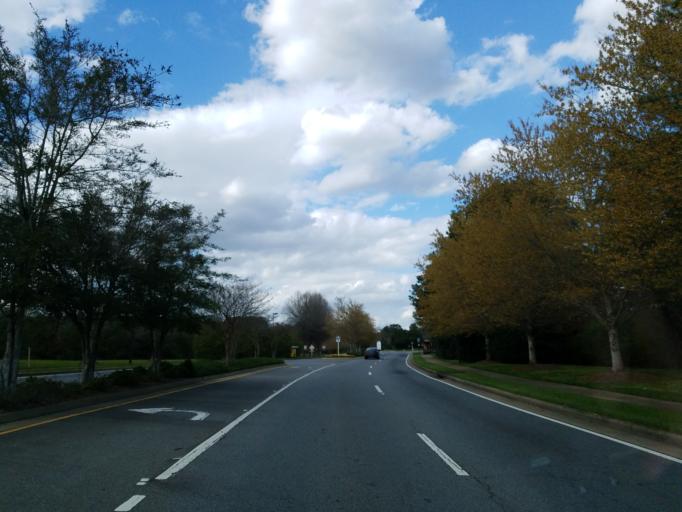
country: US
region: Georgia
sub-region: Cobb County
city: Kennesaw
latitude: 34.0296
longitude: -84.5567
